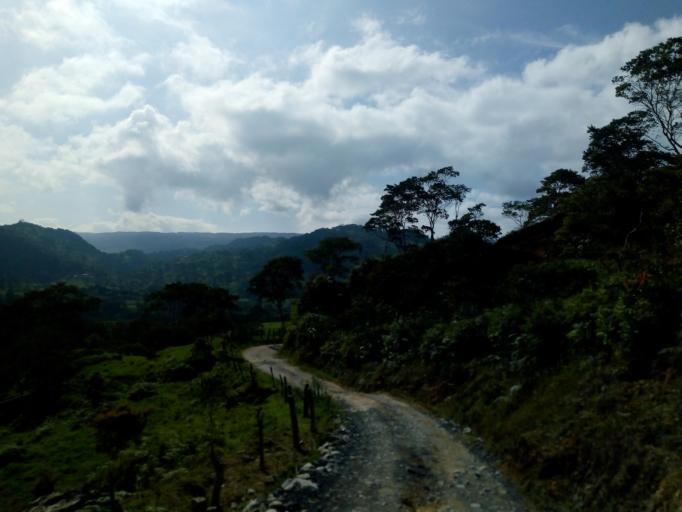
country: CO
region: Boyaca
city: Moniquira
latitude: 5.8828
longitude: -73.5088
